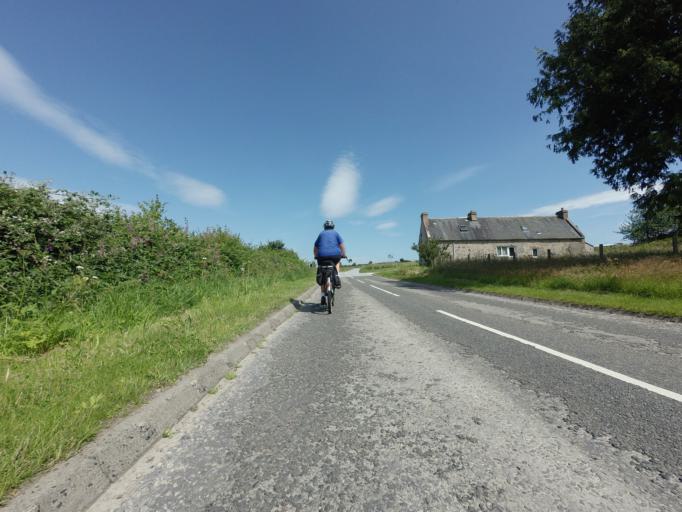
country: GB
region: Scotland
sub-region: Highland
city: Conon Bridge
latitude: 57.5522
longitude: -4.4047
